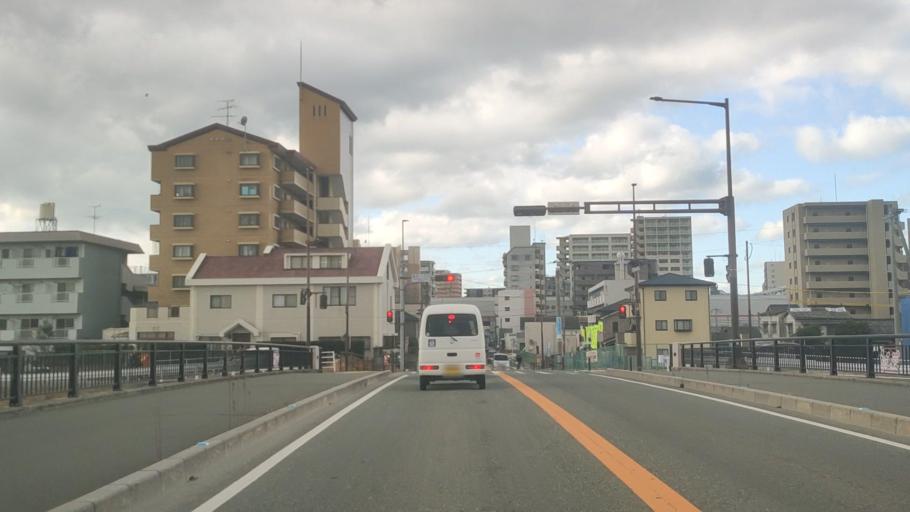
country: JP
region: Fukuoka
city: Fukuoka-shi
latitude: 33.6169
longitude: 130.4298
